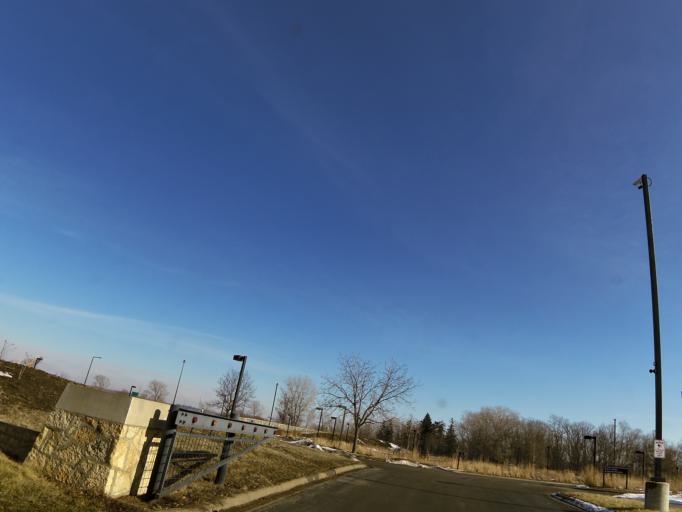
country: US
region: Minnesota
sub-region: Hennepin County
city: Richfield
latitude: 44.8606
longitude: -93.2173
